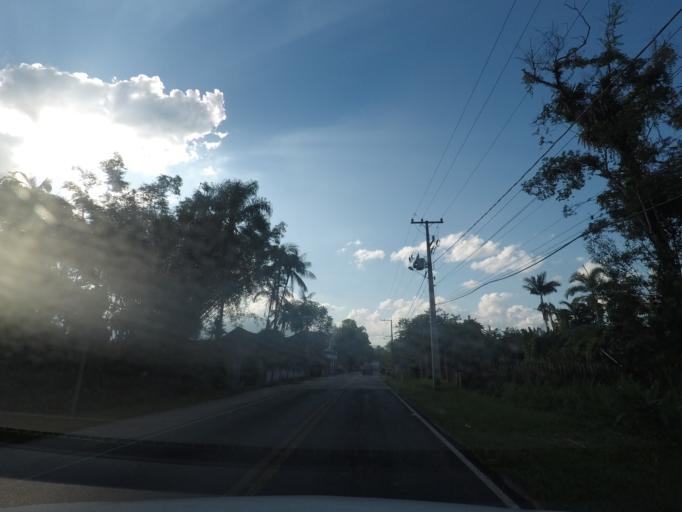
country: BR
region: Parana
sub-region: Antonina
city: Antonina
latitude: -25.4381
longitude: -48.8761
